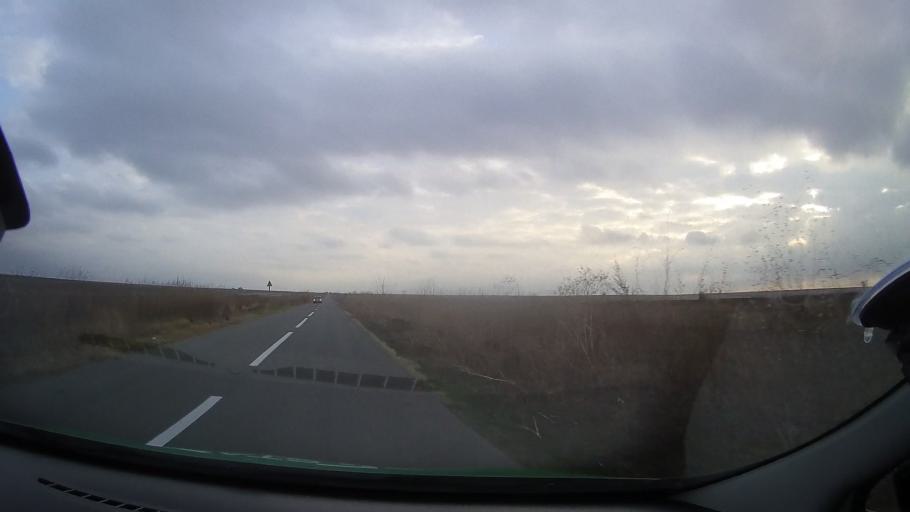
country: RO
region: Constanta
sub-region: Comuna Pestera
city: Pestera
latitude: 44.1506
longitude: 28.1139
